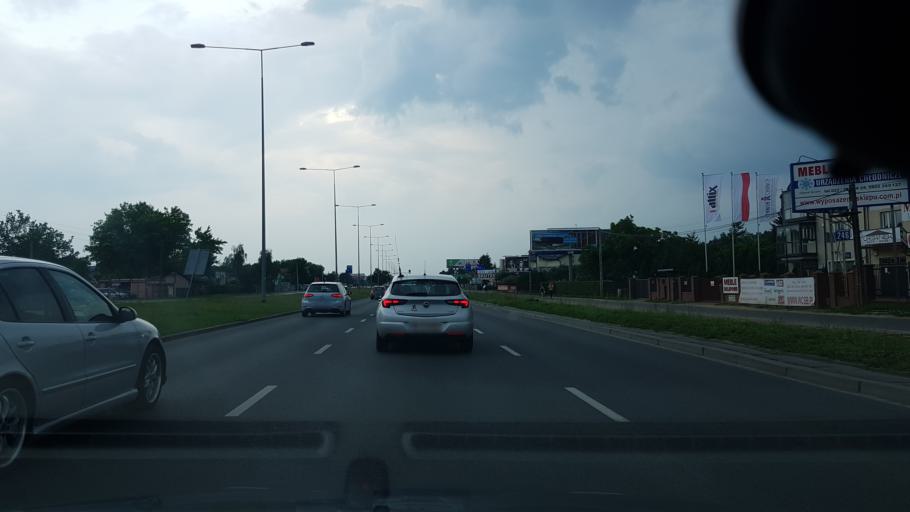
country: PL
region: Masovian Voivodeship
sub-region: Warszawa
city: Bialoleka
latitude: 52.3363
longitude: 20.9602
